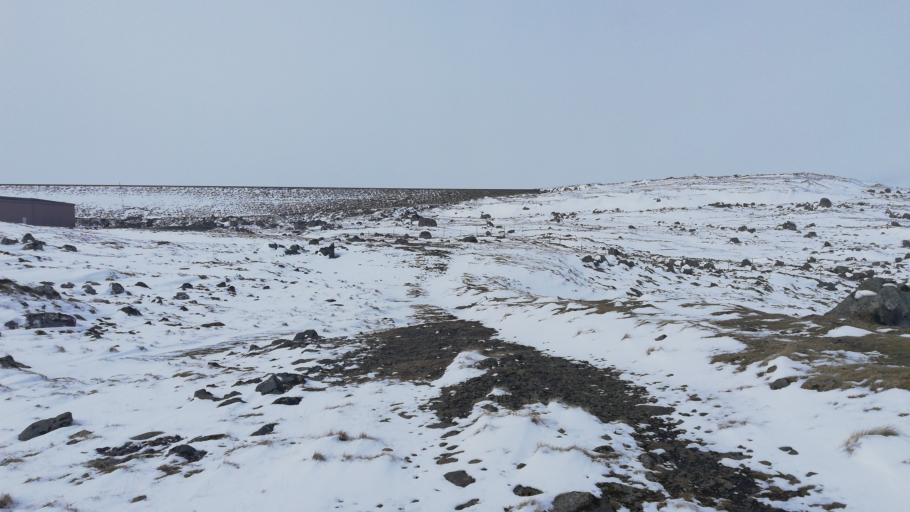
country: FO
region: Streymoy
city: Hoyvik
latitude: 62.0308
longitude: -6.8126
